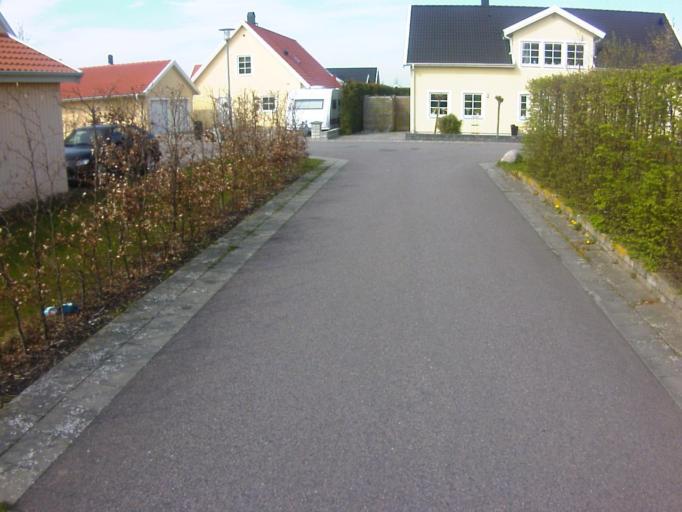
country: SE
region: Skane
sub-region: Kavlinge Kommun
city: Loddekopinge
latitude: 55.7662
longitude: 13.0224
